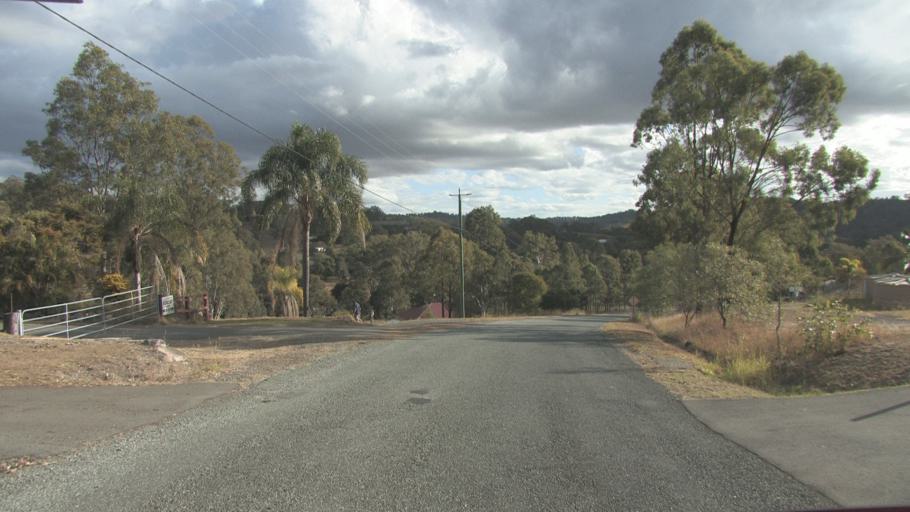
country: AU
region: Queensland
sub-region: Logan
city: Cedar Vale
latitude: -27.9015
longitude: 153.0714
